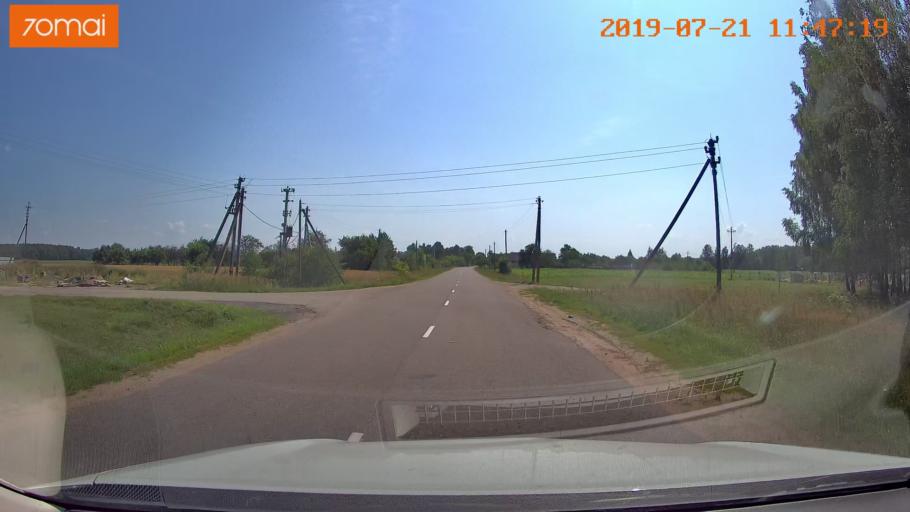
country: BY
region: Grodnenskaya
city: Lyubcha
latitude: 53.9032
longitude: 26.0454
